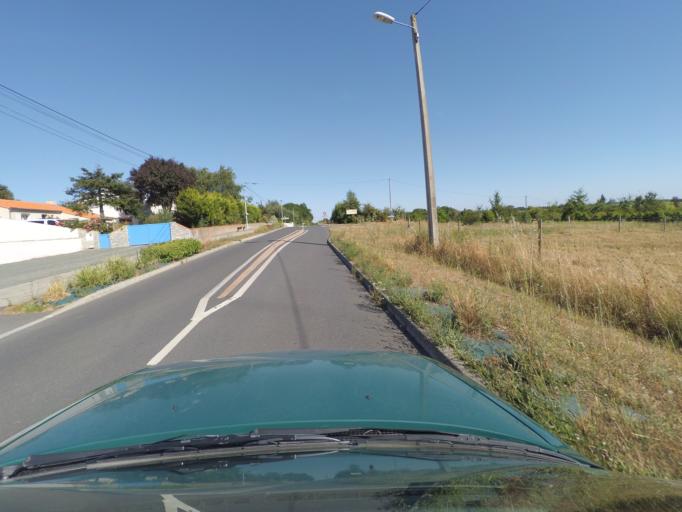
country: FR
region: Pays de la Loire
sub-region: Departement de la Loire-Atlantique
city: Maisdon-sur-Sevre
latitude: 47.0940
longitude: -1.3761
